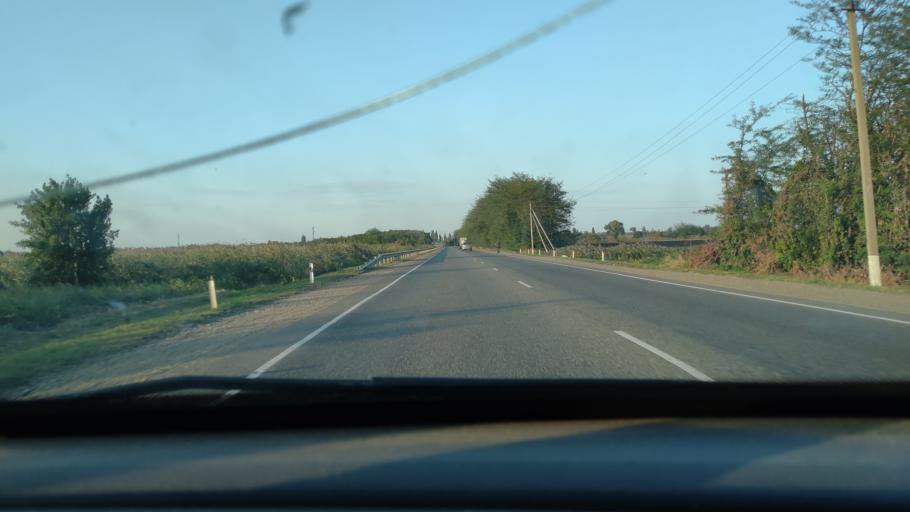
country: RU
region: Krasnodarskiy
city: Kanevskaya
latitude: 46.0669
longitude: 39.0091
